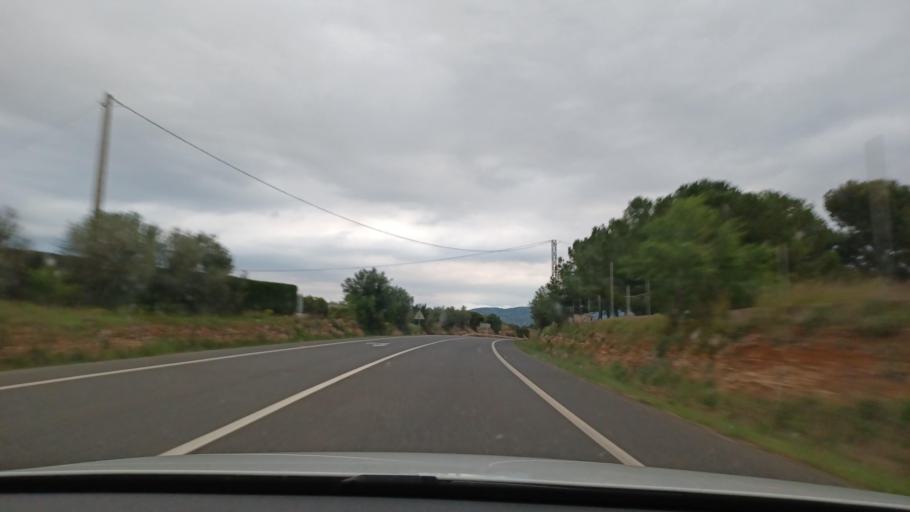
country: ES
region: Catalonia
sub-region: Provincia de Tarragona
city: Amposta
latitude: 40.7173
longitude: 0.5631
